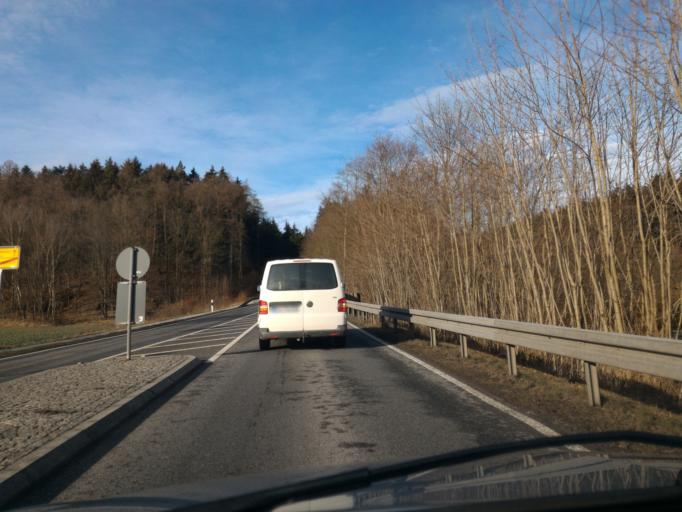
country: DE
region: Saxony
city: Steinigtwolmsdorf
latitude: 51.0563
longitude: 14.3700
